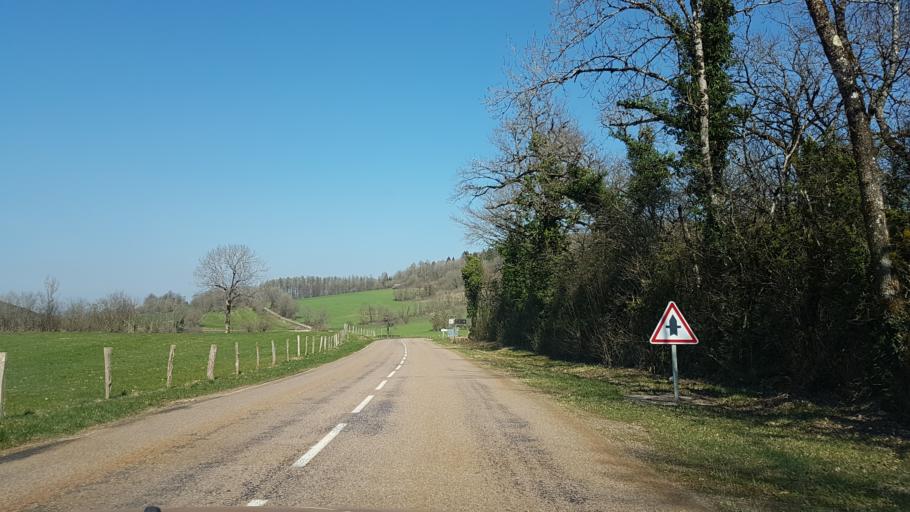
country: FR
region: Franche-Comte
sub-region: Departement du Jura
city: Orgelet
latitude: 46.5426
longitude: 5.6523
